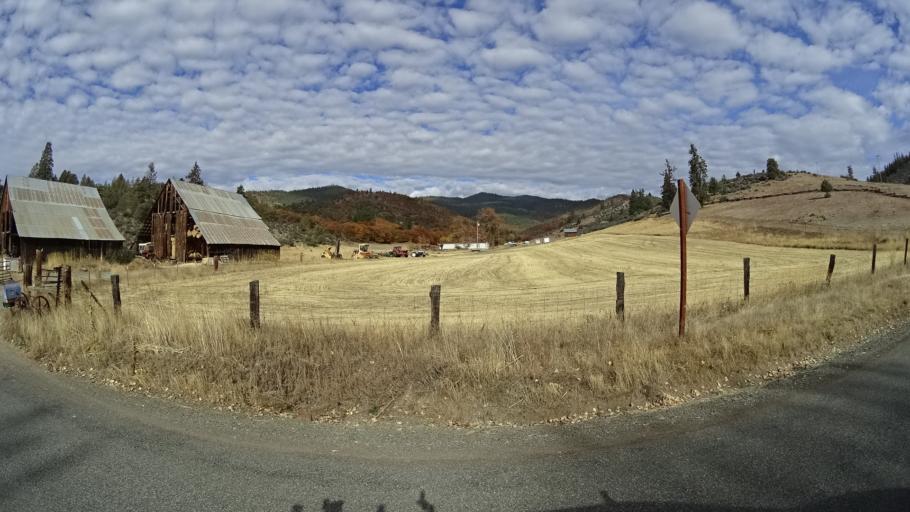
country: US
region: California
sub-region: Siskiyou County
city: Yreka
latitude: 41.6332
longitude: -122.7534
